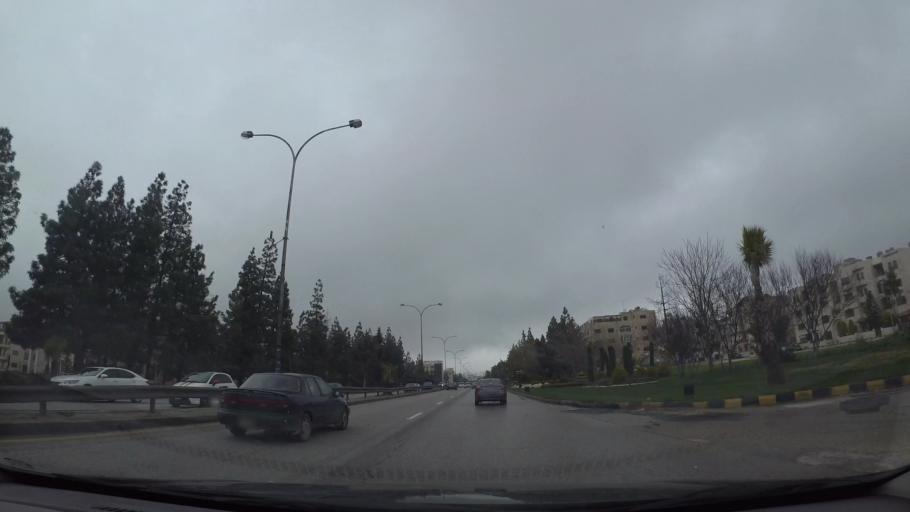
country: JO
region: Amman
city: Wadi as Sir
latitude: 31.9496
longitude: 35.8592
